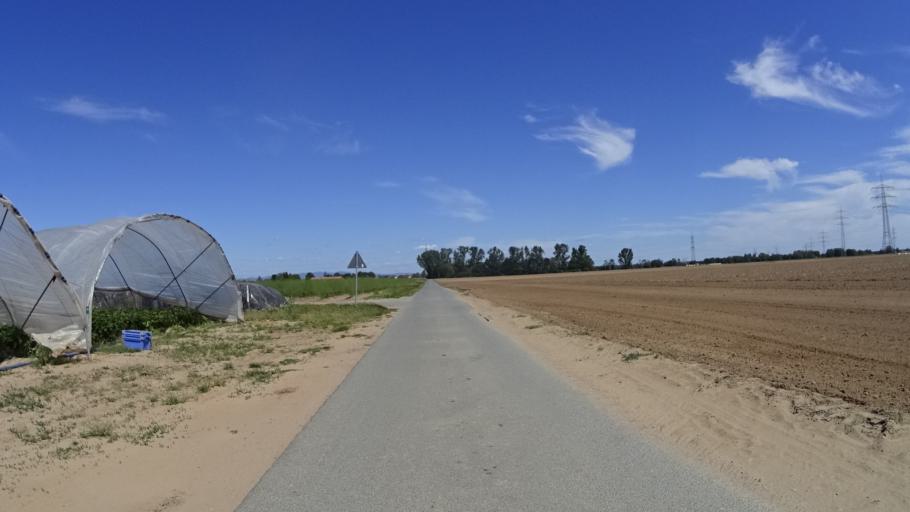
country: DE
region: Hesse
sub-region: Regierungsbezirk Darmstadt
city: Buttelborn
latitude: 49.9162
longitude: 8.5502
